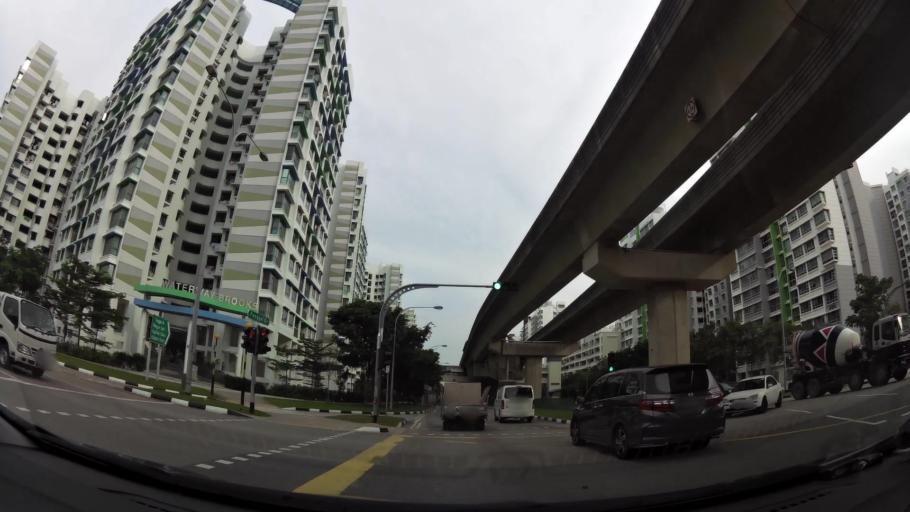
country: MY
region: Johor
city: Kampung Pasir Gudang Baru
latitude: 1.4060
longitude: 103.9078
